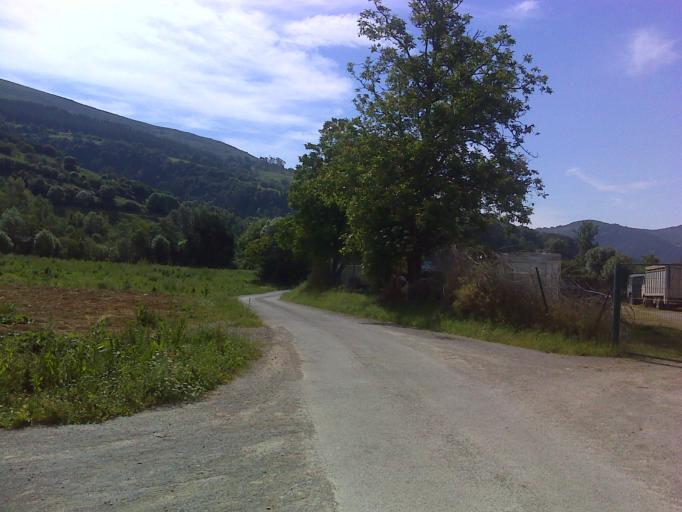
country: ES
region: Cantabria
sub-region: Provincia de Cantabria
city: Santiurde de Toranzo
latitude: 43.1941
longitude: -3.9115
